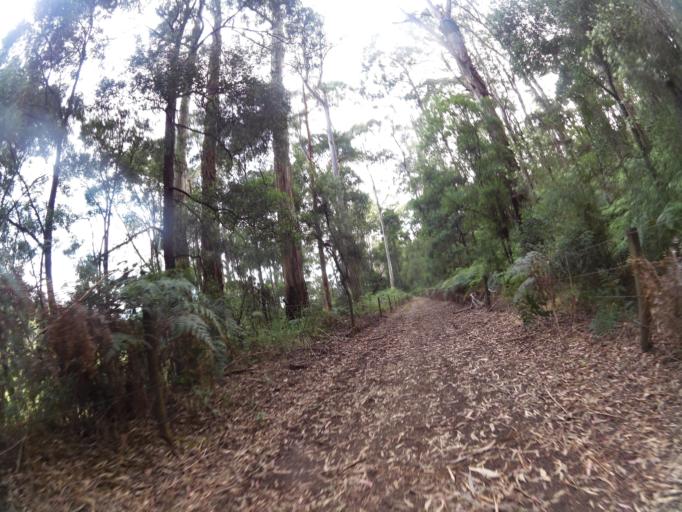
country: AU
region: Victoria
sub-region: Colac-Otway
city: Colac
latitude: -38.4966
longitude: 143.7329
